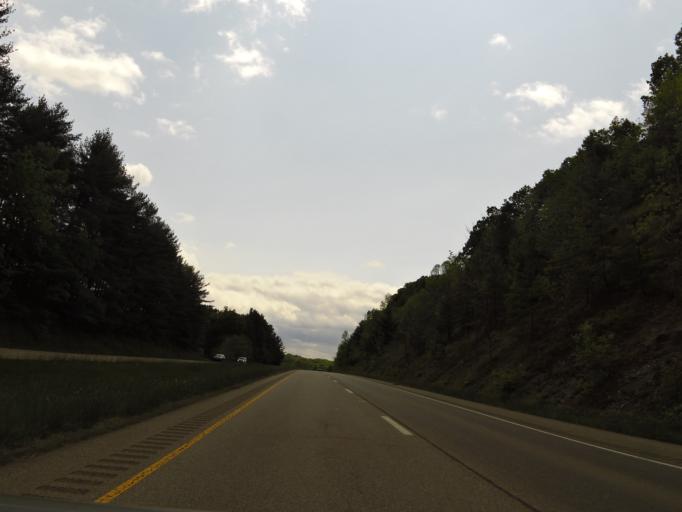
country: US
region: Ohio
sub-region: Meigs County
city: Pomeroy
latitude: 39.1071
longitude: -82.0140
